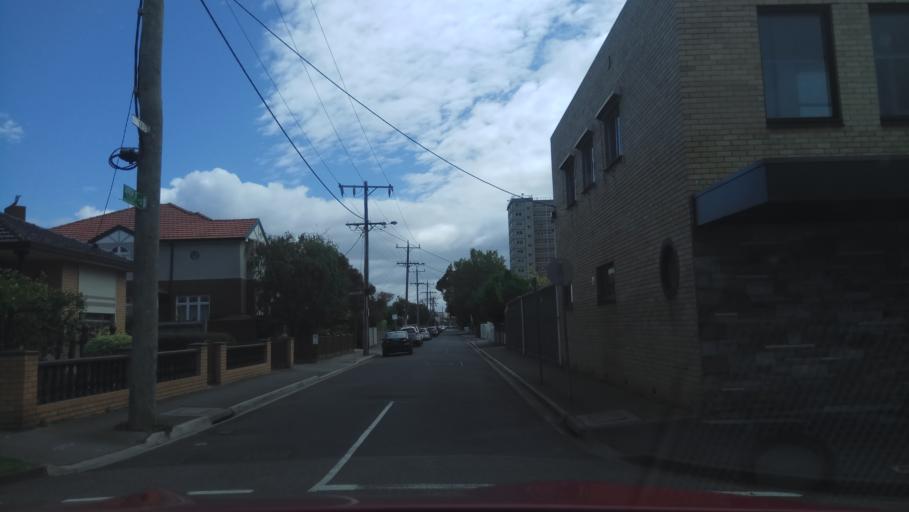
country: AU
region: Victoria
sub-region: Hobsons Bay
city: Williamstown
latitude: -37.8630
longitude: 144.9018
